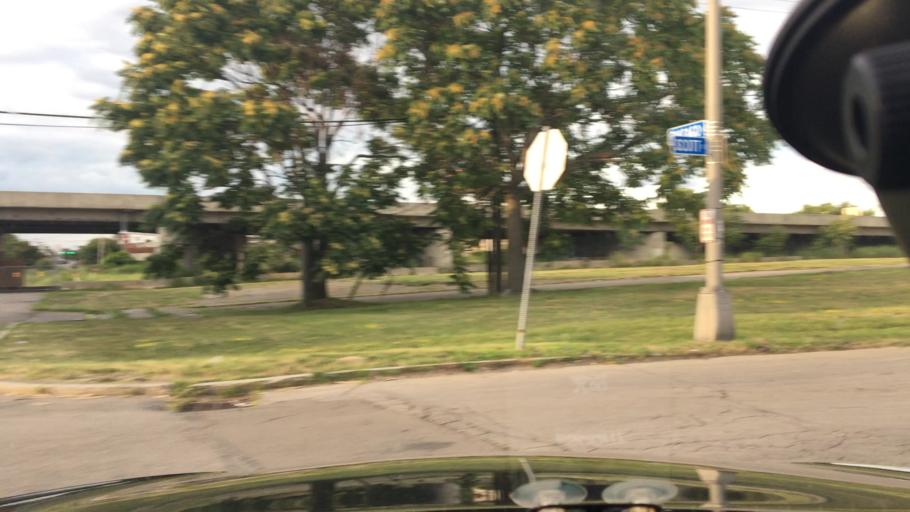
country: US
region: New York
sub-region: Erie County
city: Buffalo
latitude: 42.8755
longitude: -78.8670
